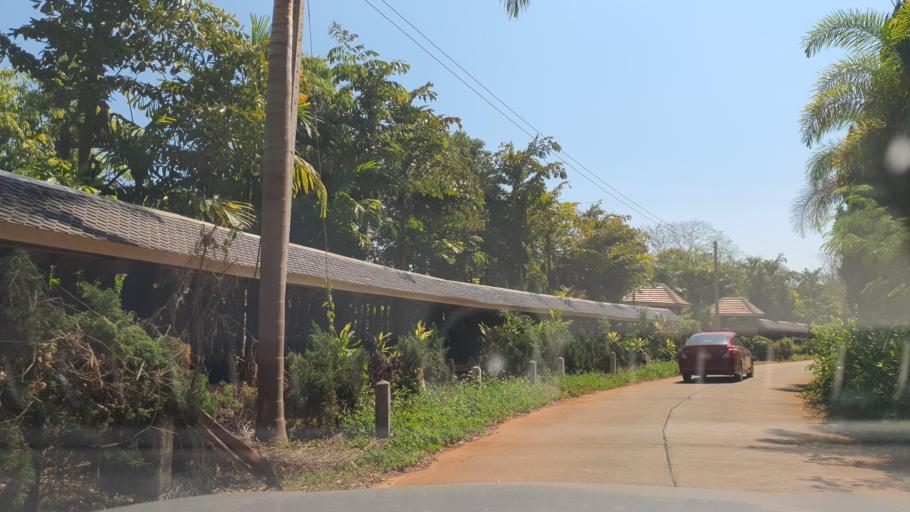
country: TH
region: Lampang
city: Wang Nuea
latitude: 19.1841
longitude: 99.5004
